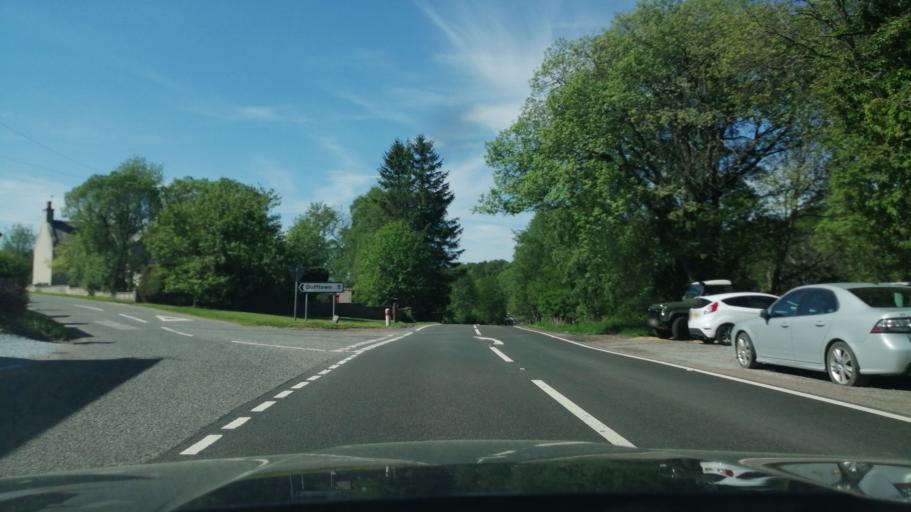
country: GB
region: Scotland
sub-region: Moray
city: Dufftown
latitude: 57.4984
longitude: -3.1404
